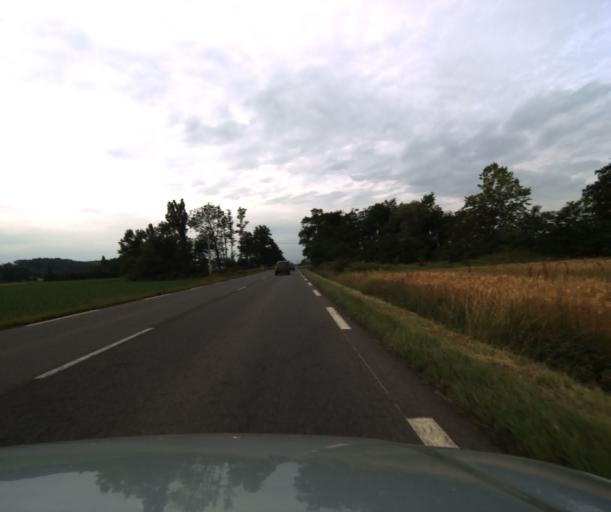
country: FR
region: Midi-Pyrenees
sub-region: Departement des Hautes-Pyrenees
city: Rabastens-de-Bigorre
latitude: 43.3635
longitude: 0.1417
